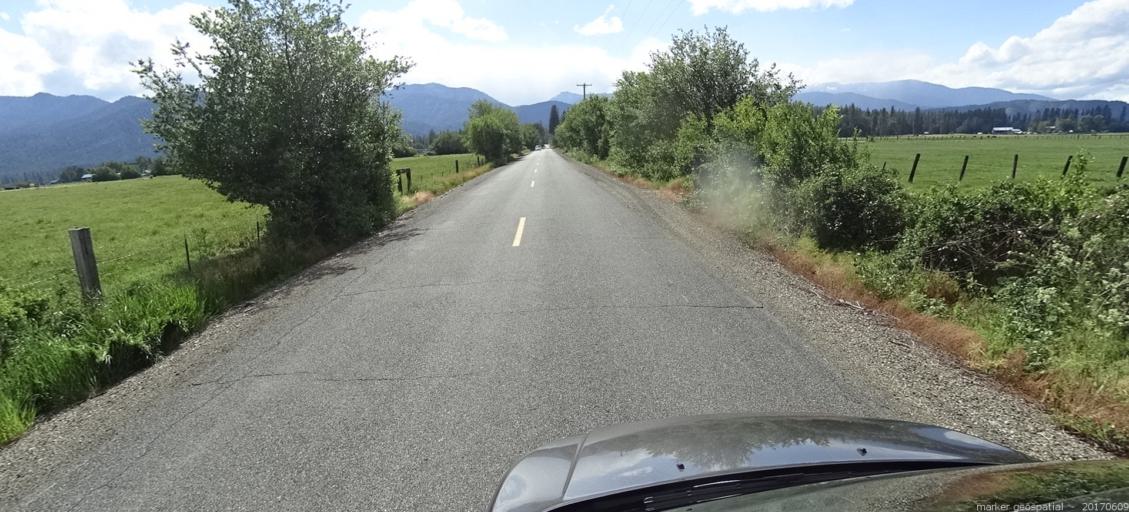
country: US
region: California
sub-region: Siskiyou County
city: Yreka
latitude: 41.5152
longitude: -122.8915
